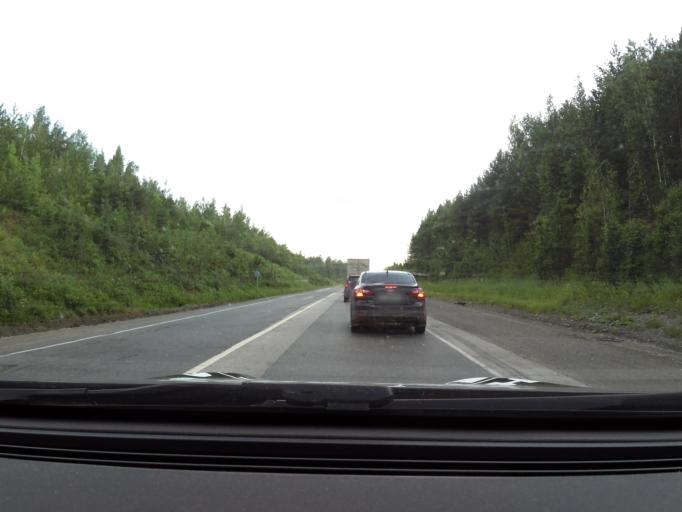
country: RU
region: Sverdlovsk
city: Talitsa
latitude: 56.8321
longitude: 59.9962
